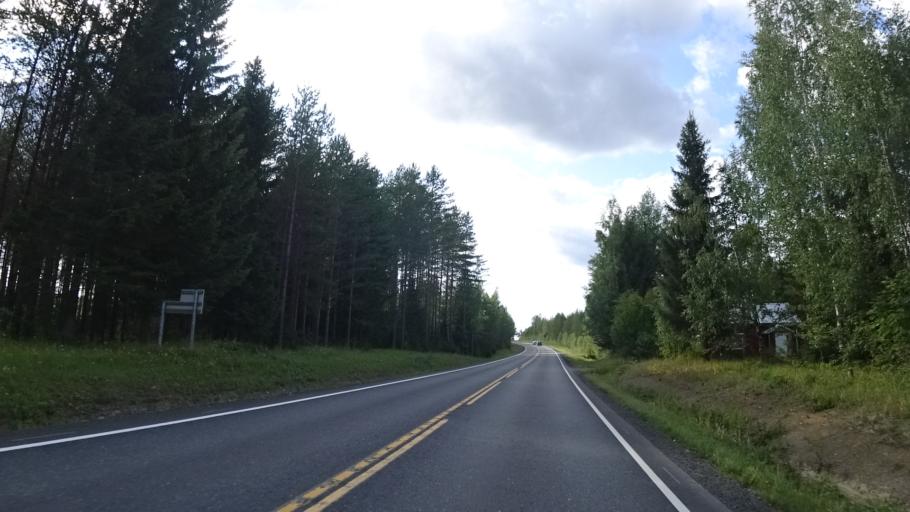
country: FI
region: North Karelia
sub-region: Keski-Karjala
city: Tohmajaervi
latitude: 62.1847
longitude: 30.5025
